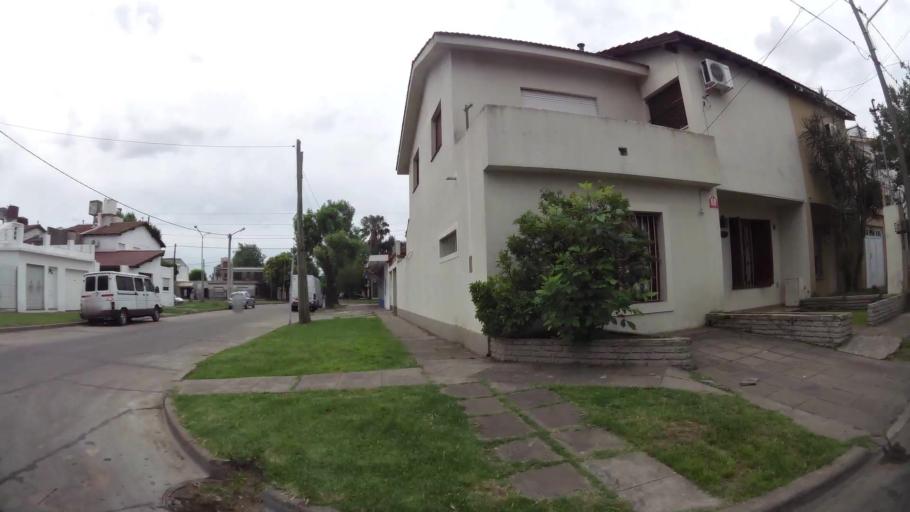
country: AR
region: Buenos Aires
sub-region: Partido de Campana
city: Campana
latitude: -34.1757
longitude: -58.9660
